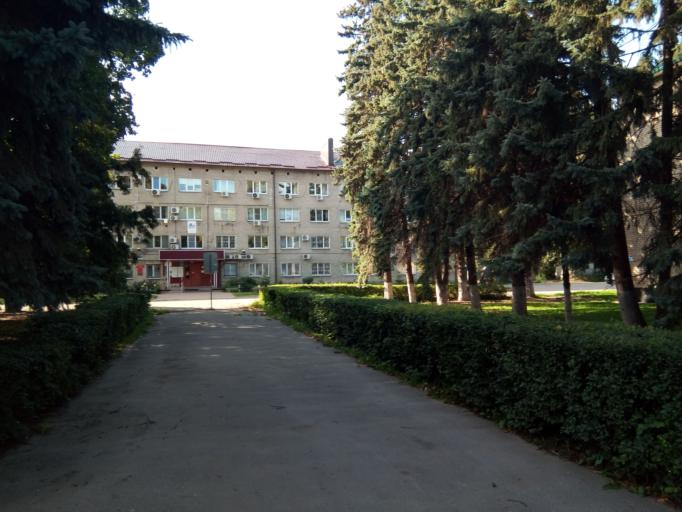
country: RU
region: Lipetsk
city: Lipetsk
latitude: 52.6303
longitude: 39.5539
